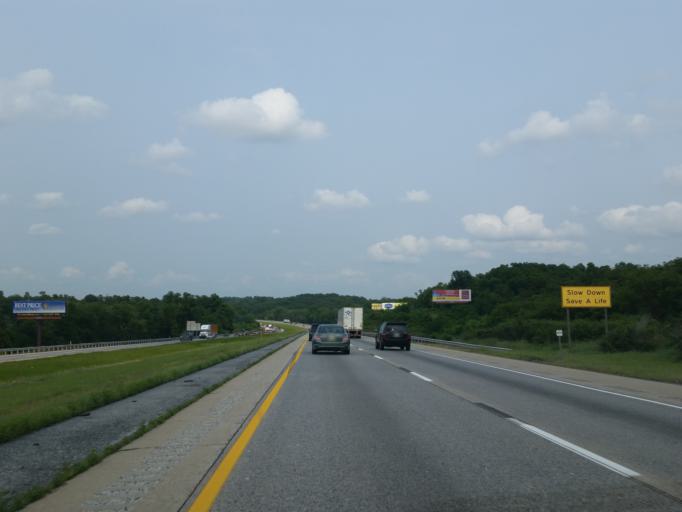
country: US
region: Pennsylvania
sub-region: Dauphin County
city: Linglestown
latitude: 40.3298
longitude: -76.7708
